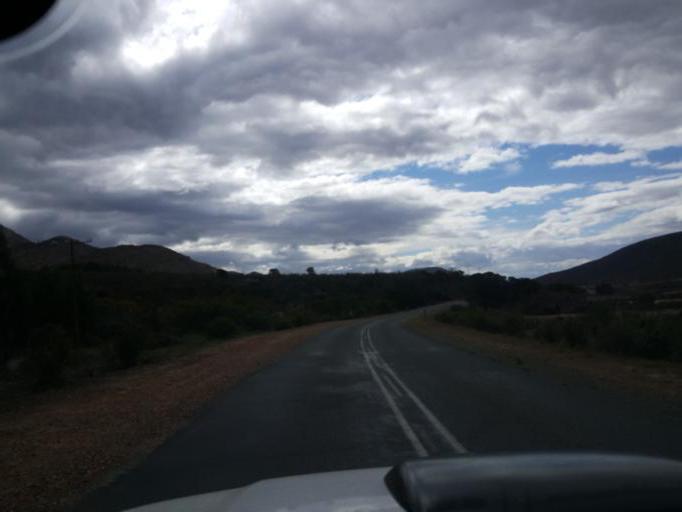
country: ZA
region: Western Cape
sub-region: Eden District Municipality
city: George
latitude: -33.8258
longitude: 22.3901
